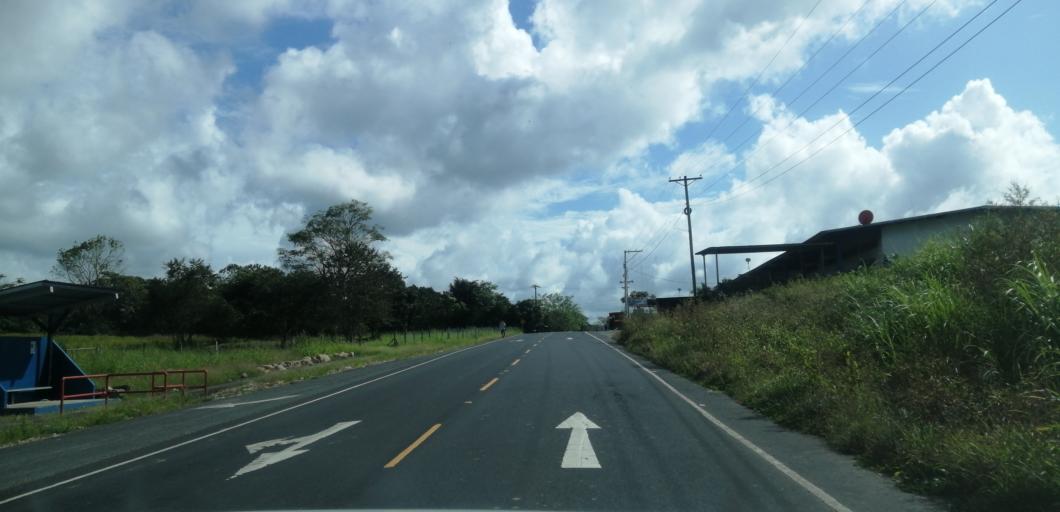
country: PA
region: Panama
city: Canita
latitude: 9.2211
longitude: -78.8980
